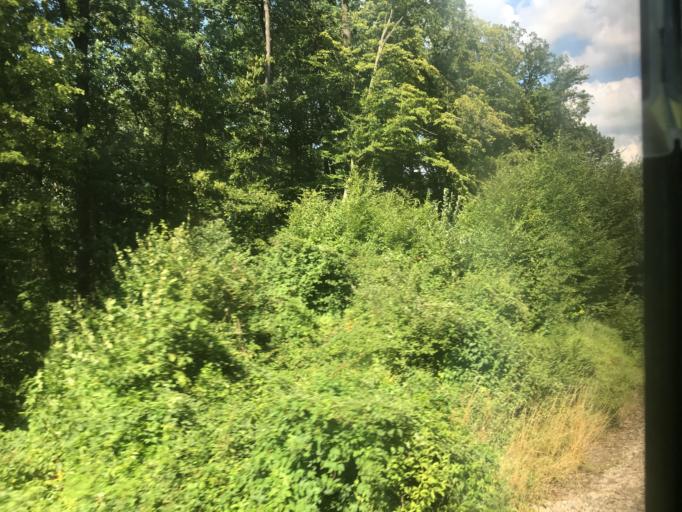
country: AT
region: Upper Austria
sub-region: Politischer Bezirk Urfahr-Umgebung
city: Engerwitzdorf
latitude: 48.3198
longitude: 14.5081
